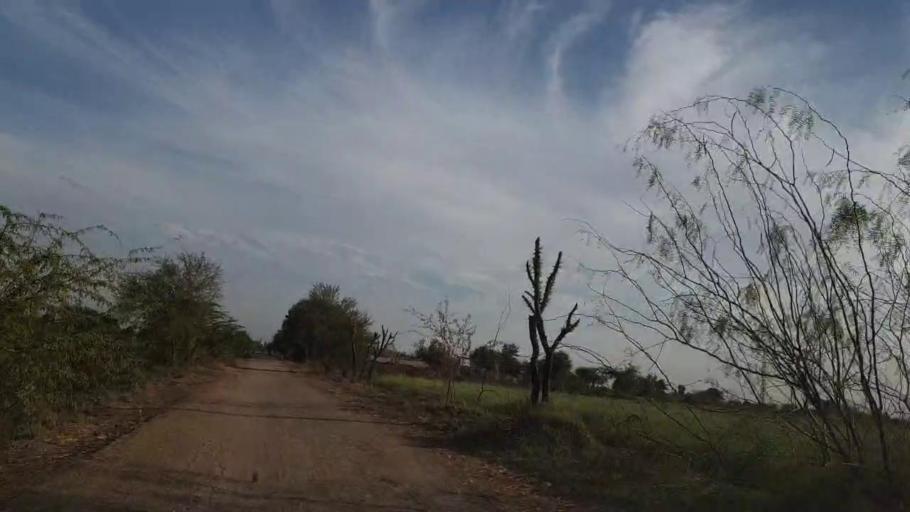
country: PK
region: Sindh
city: Pithoro
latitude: 25.6472
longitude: 69.3011
